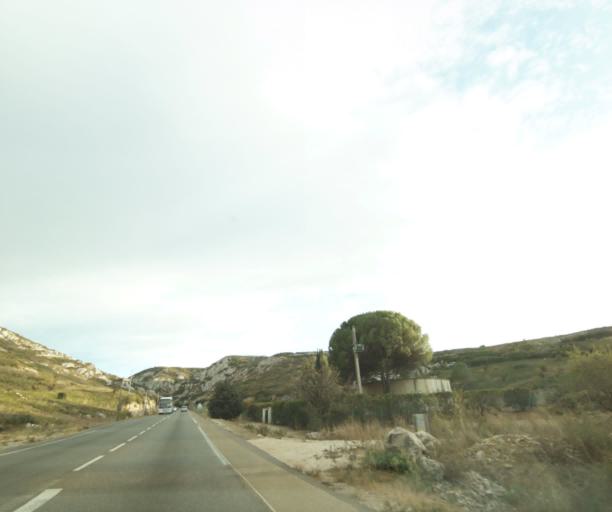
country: FR
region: Provence-Alpes-Cote d'Azur
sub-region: Departement des Bouches-du-Rhone
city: Gignac-la-Nerthe
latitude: 43.3749
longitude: 5.2282
